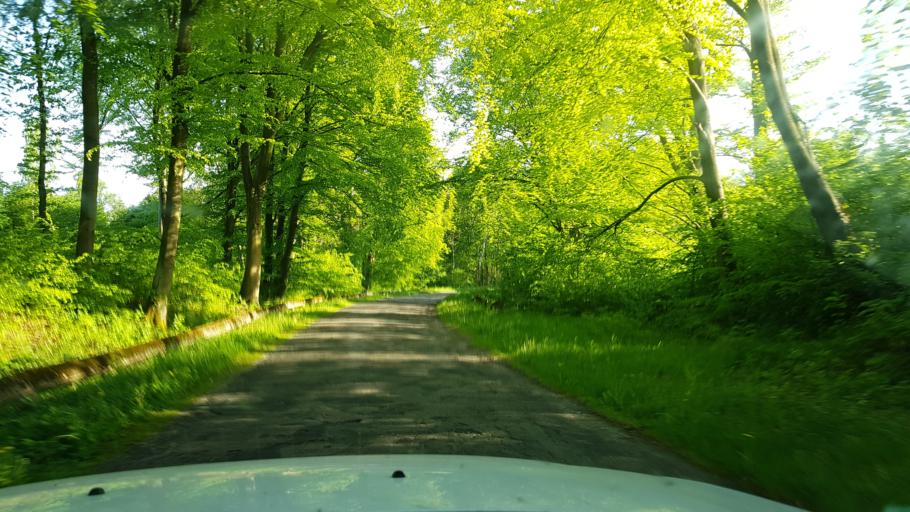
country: PL
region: West Pomeranian Voivodeship
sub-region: Powiat lobeski
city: Dobra
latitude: 53.5958
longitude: 15.3325
